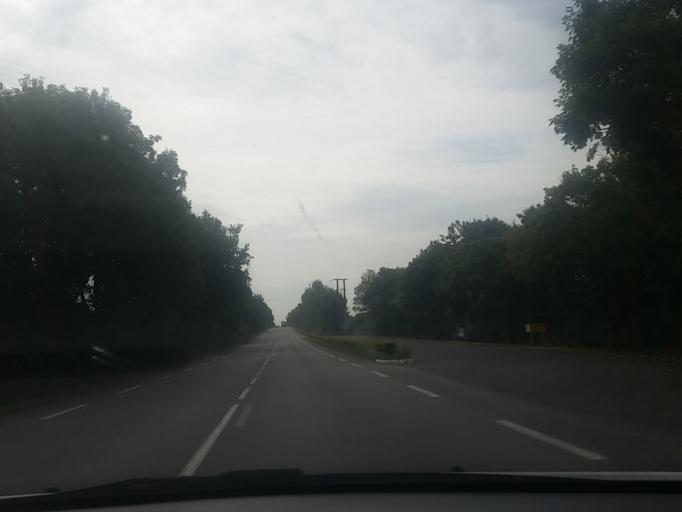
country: FR
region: Pays de la Loire
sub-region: Departement de la Vendee
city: Sainte-Cecile
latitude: 46.7680
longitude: -1.1083
